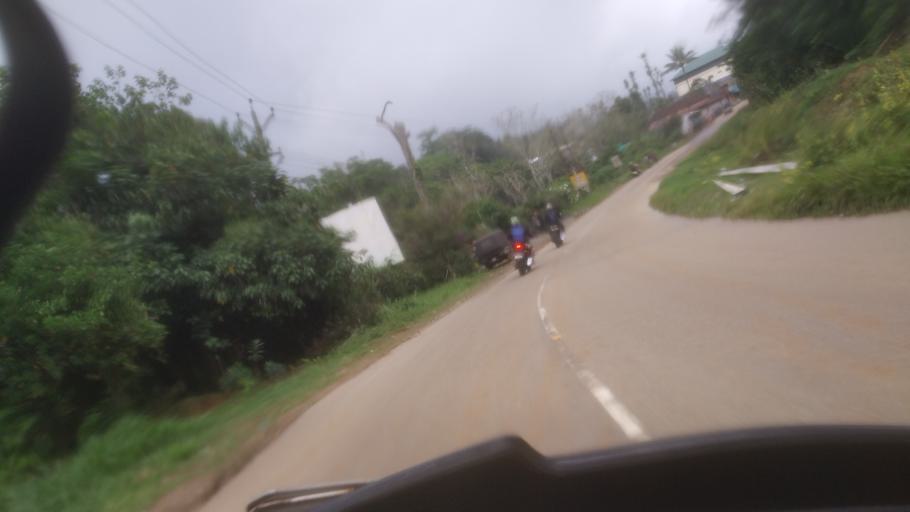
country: IN
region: Tamil Nadu
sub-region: Theni
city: Kombai
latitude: 9.8998
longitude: 77.1748
